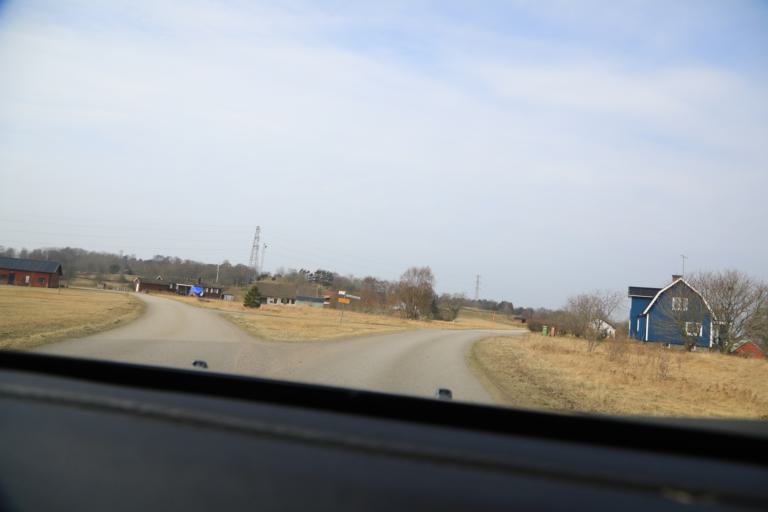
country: SE
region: Halland
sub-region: Kungsbacka Kommun
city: Frillesas
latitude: 57.2672
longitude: 12.1586
